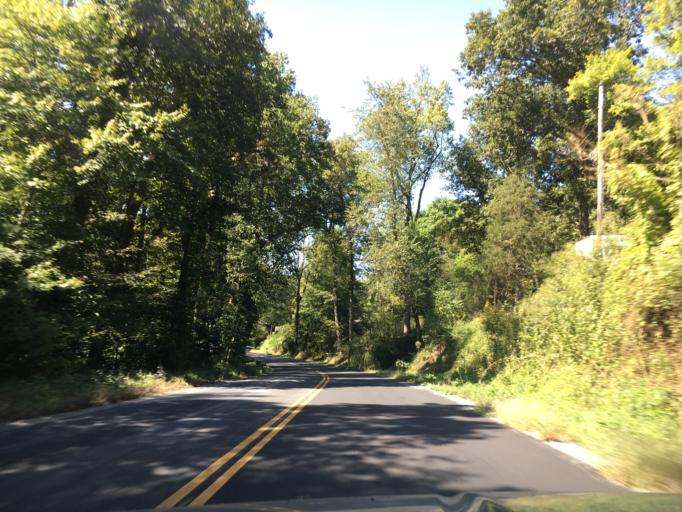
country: US
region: Virginia
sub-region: Albemarle County
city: Crozet
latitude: 37.9872
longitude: -78.7155
